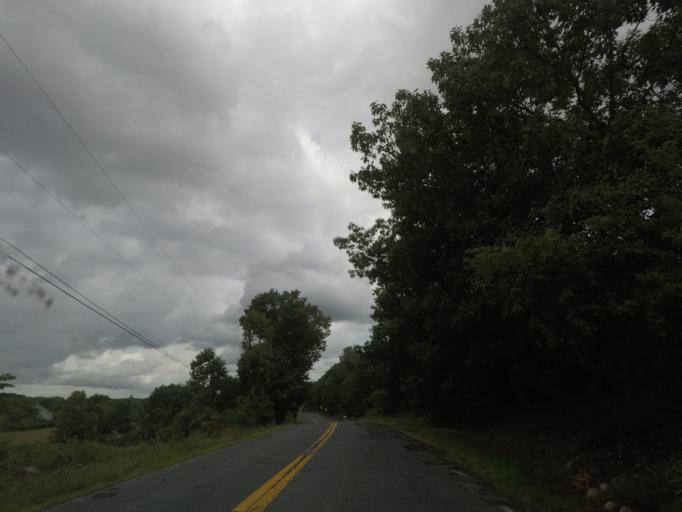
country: US
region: New York
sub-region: Rensselaer County
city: Wynantskill
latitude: 42.6765
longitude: -73.6361
